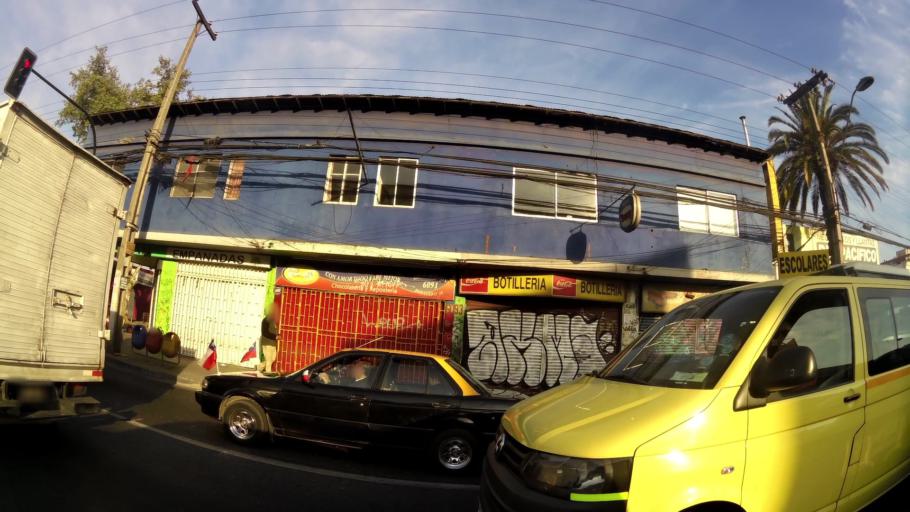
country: CL
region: Santiago Metropolitan
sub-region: Provincia de Santiago
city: Santiago
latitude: -33.5115
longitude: -70.6573
